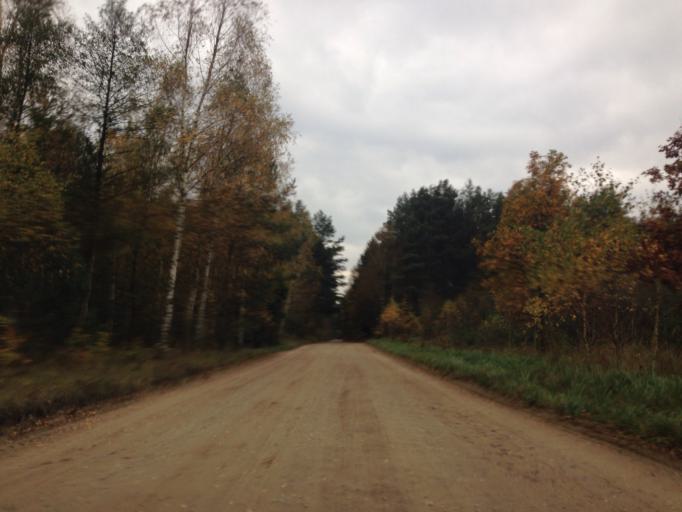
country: PL
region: Kujawsko-Pomorskie
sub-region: Powiat brodnicki
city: Bartniczka
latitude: 53.2847
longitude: 19.5835
